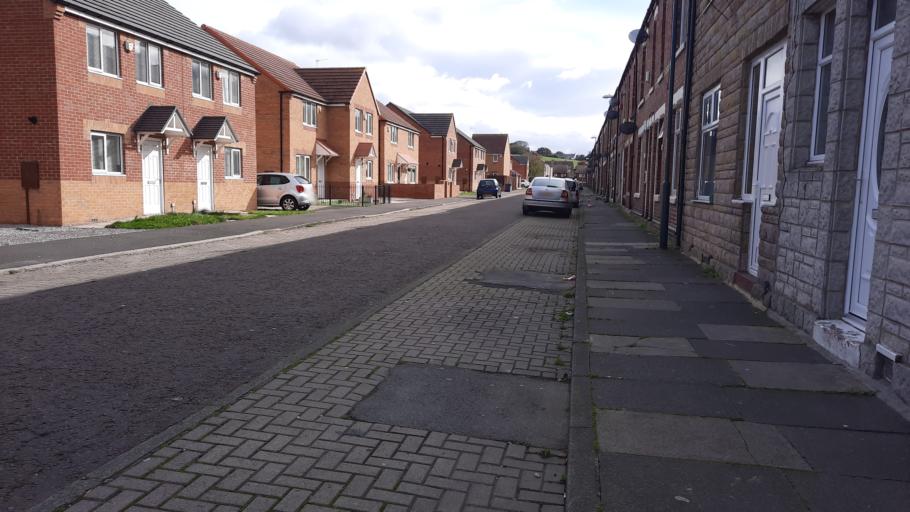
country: GB
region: England
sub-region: South Tyneside
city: The Boldons
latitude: 54.9481
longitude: -1.4591
